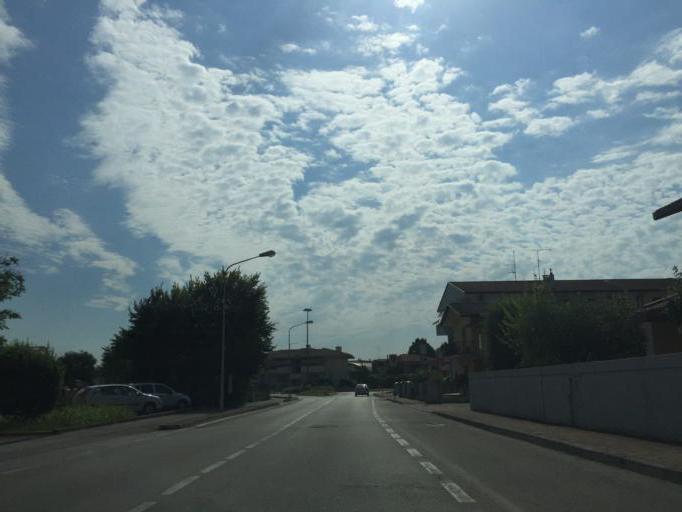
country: IT
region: Friuli Venezia Giulia
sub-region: Provincia di Pordenone
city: Sacile
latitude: 45.9556
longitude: 12.4899
